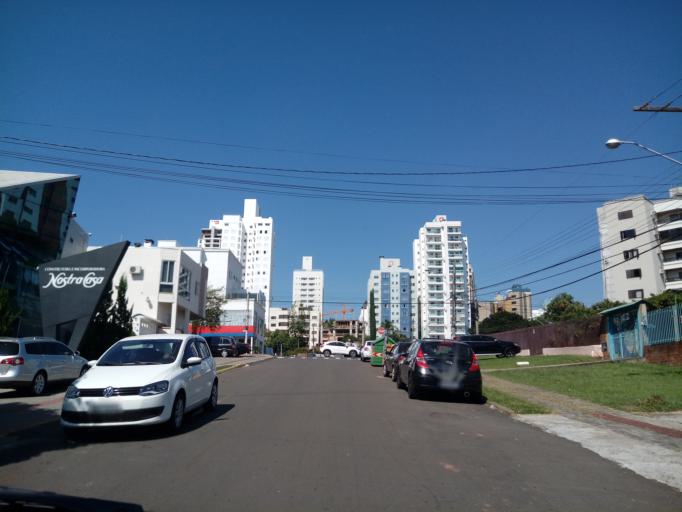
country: BR
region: Santa Catarina
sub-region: Chapeco
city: Chapeco
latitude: -27.0988
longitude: -52.6108
